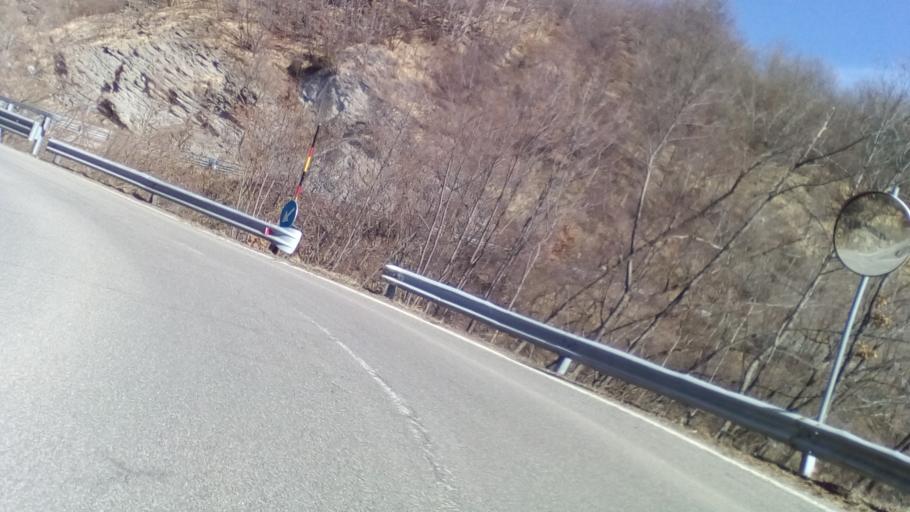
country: IT
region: Emilia-Romagna
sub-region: Provincia di Modena
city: Riolunato
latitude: 44.2555
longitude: 10.6347
